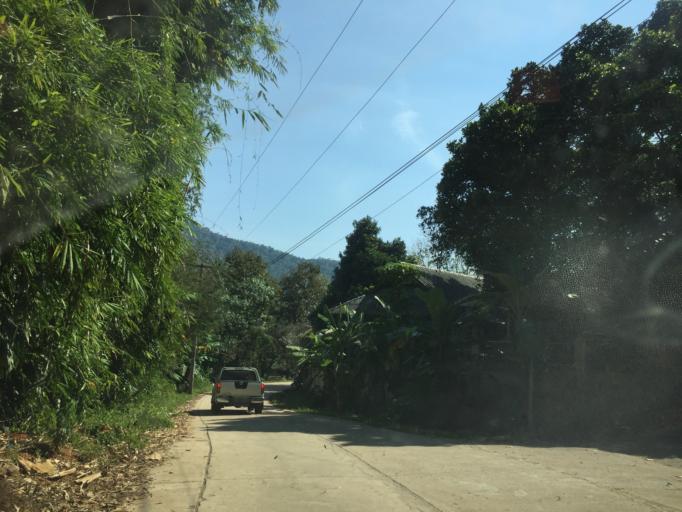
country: TH
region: Chiang Mai
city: Samoeng
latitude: 18.9886
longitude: 98.7271
